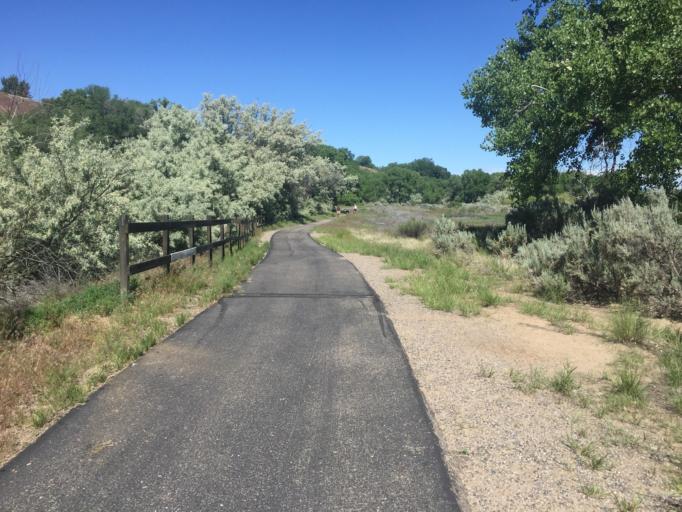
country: US
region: Colorado
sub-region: Mesa County
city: Redlands
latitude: 39.0690
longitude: -108.5963
